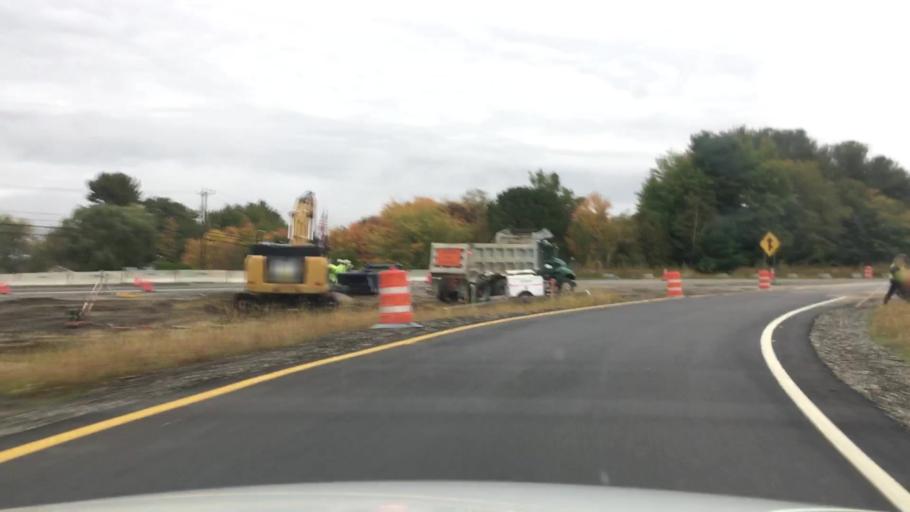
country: US
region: Maine
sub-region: York County
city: Eliot
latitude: 43.1328
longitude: -70.8369
